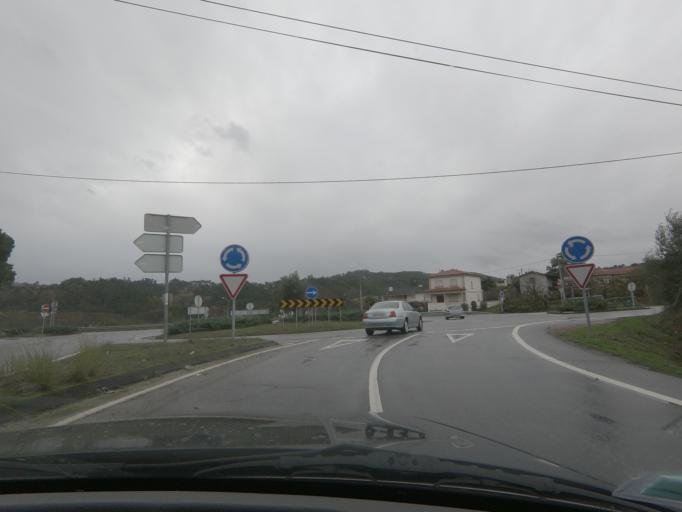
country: PT
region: Porto
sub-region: Amarante
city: Teloes
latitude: 41.3204
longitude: -8.0676
